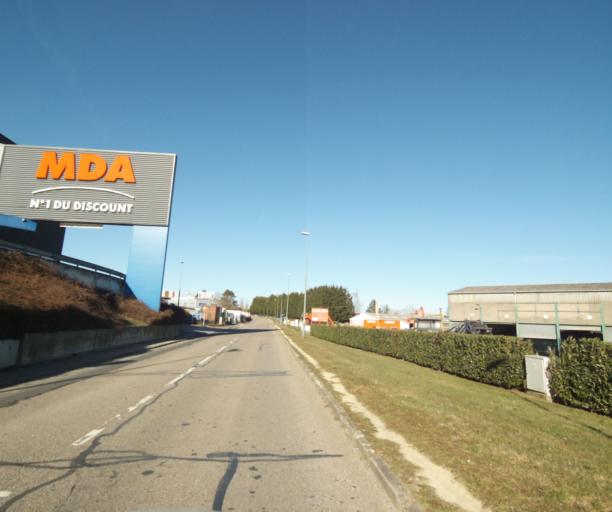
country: FR
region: Lorraine
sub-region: Departement de Meurthe-et-Moselle
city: Vandoeuvre-les-Nancy
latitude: 48.6442
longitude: 6.1849
